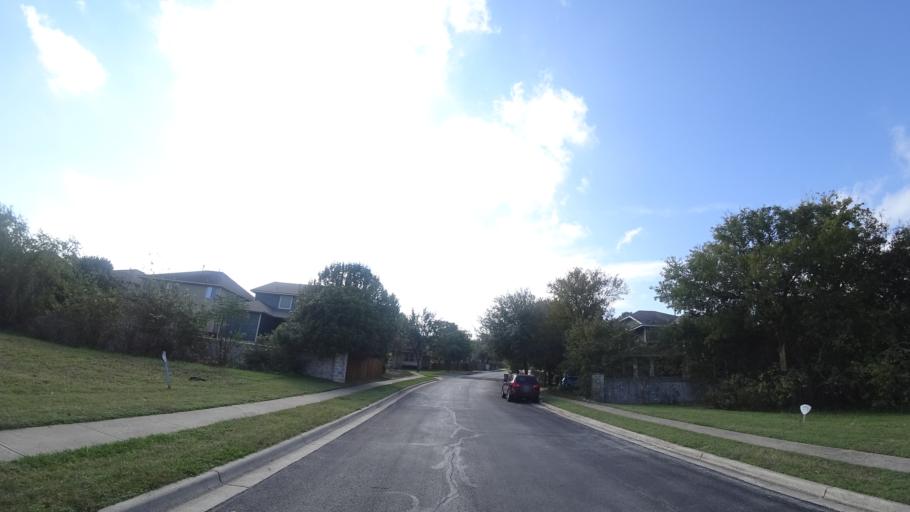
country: US
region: Texas
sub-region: Travis County
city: Manchaca
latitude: 30.1897
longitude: -97.8170
